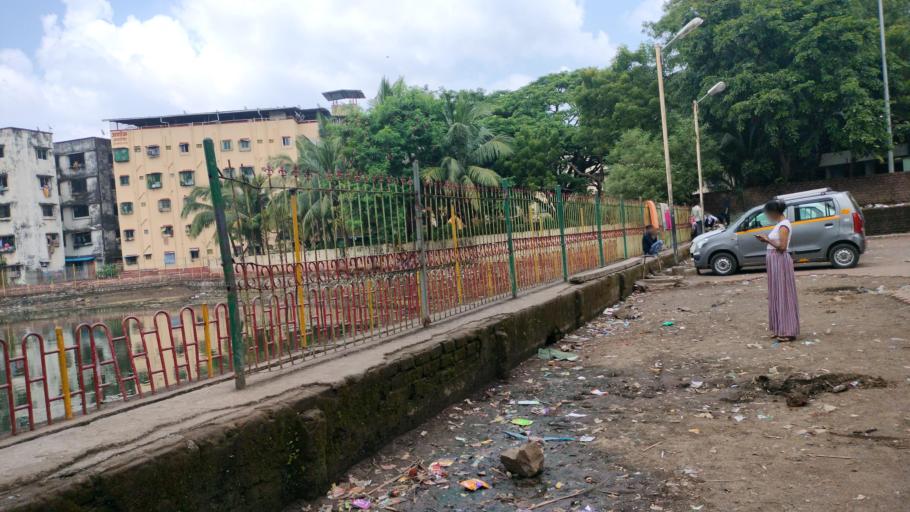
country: IN
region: Maharashtra
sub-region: Thane
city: Virar
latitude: 19.4664
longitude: 72.8125
